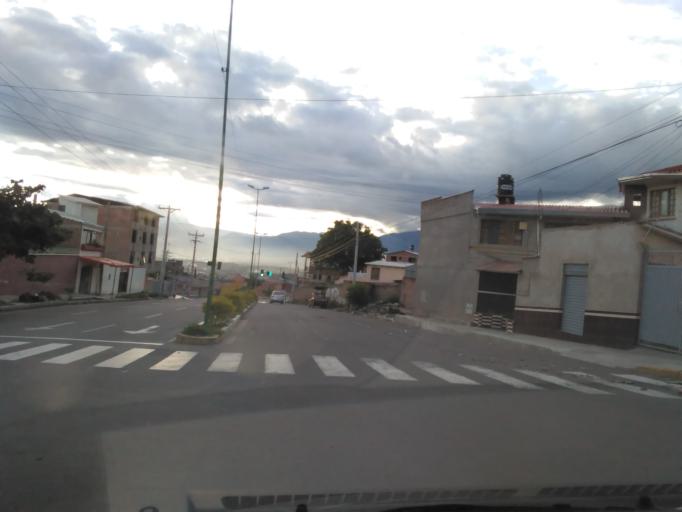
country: BO
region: Cochabamba
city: Cochabamba
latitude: -17.3507
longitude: -66.1677
